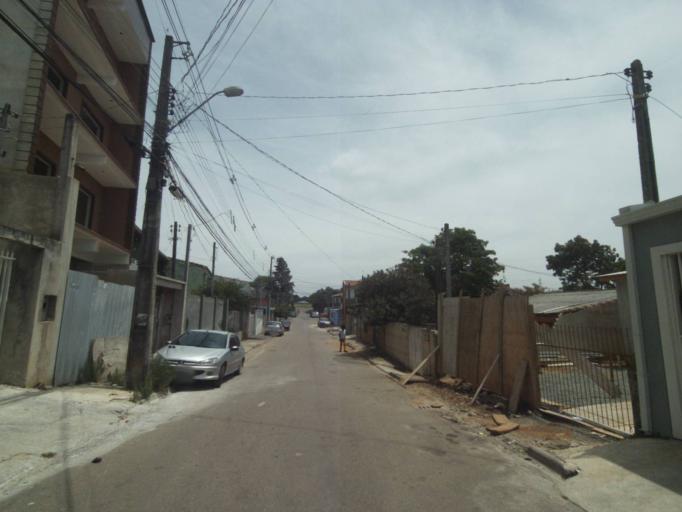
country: BR
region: Parana
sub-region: Curitiba
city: Curitiba
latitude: -25.5032
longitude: -49.3394
